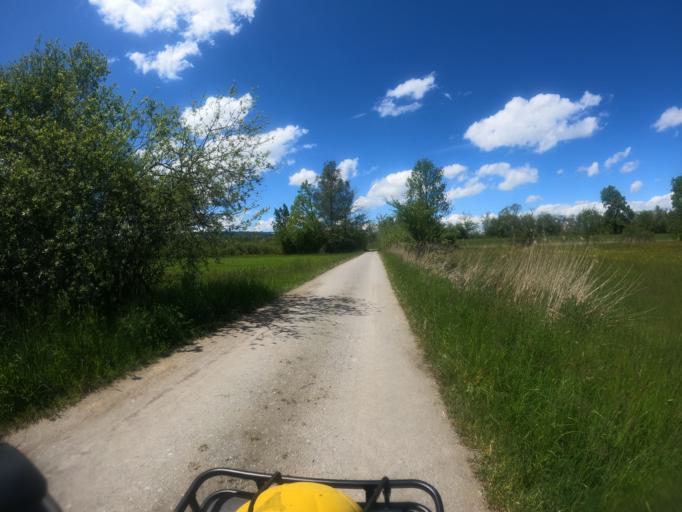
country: CH
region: Zurich
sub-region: Bezirk Affoltern
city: Obfelden / Oberlunnern
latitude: 47.2346
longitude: 8.4066
